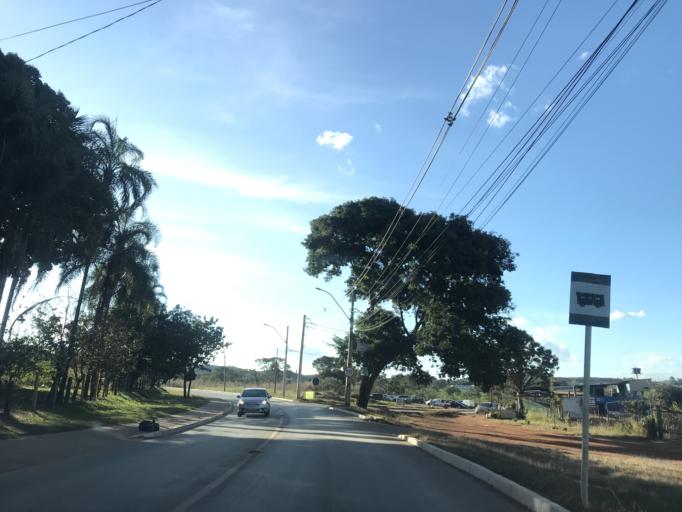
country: BR
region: Federal District
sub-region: Brasilia
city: Brasilia
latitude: -15.8861
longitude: -47.7804
